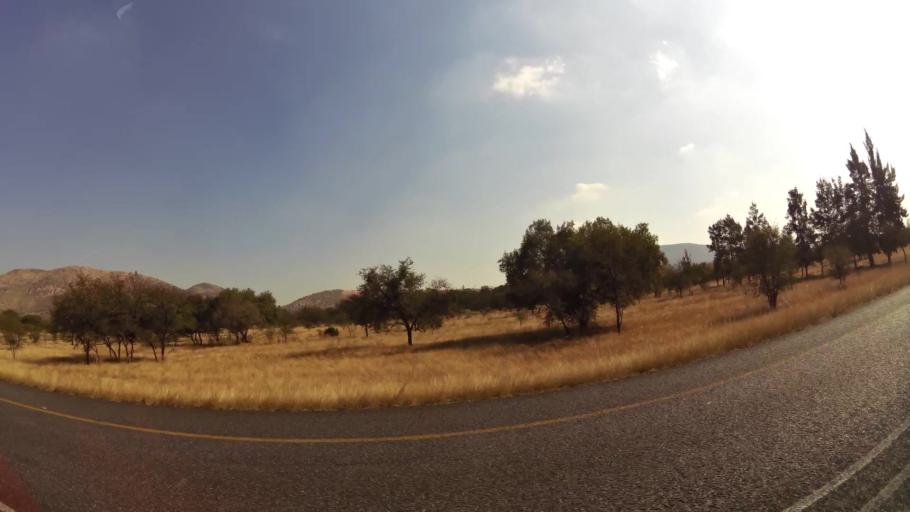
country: ZA
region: North-West
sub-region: Bojanala Platinum District Municipality
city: Rustenburg
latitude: -25.6269
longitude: 27.1577
